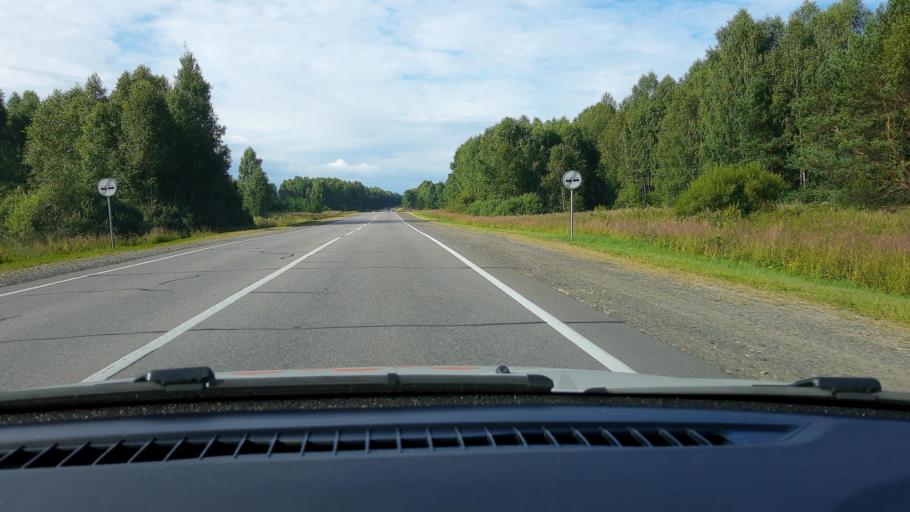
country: RU
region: Nizjnij Novgorod
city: Arzamas
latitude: 55.5477
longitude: 43.9392
